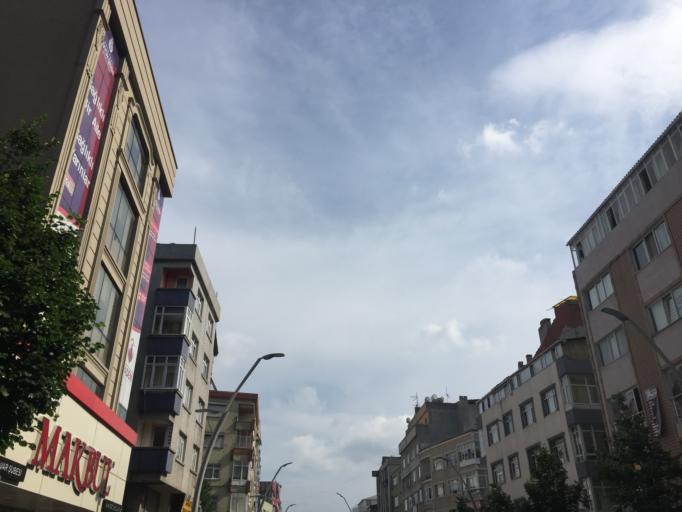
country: TR
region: Istanbul
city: Zeytinburnu
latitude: 40.9928
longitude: 28.9039
